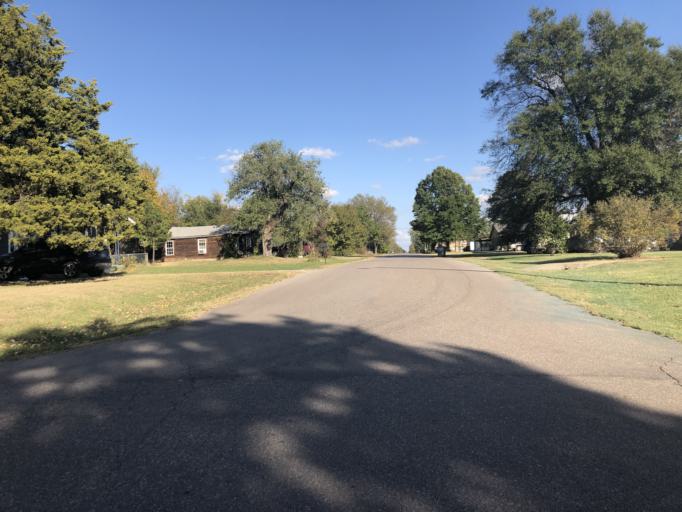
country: US
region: Oklahoma
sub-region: Pottawatomie County
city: Tecumseh
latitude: 35.2555
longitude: -96.9394
